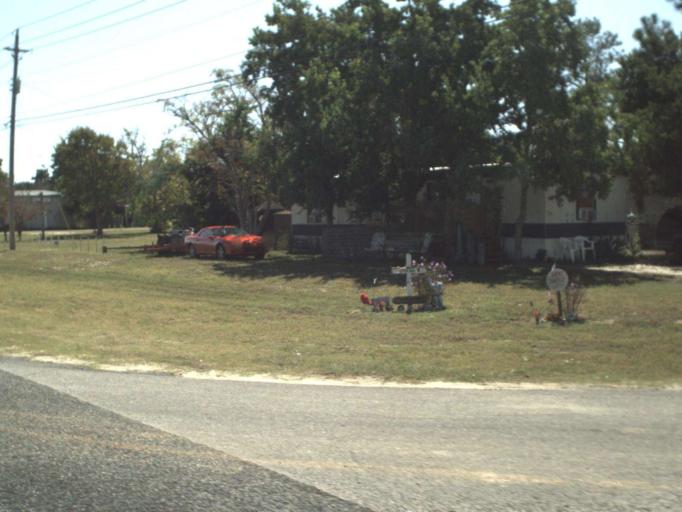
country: US
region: Florida
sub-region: Bay County
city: Laguna Beach
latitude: 30.2436
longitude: -85.9195
